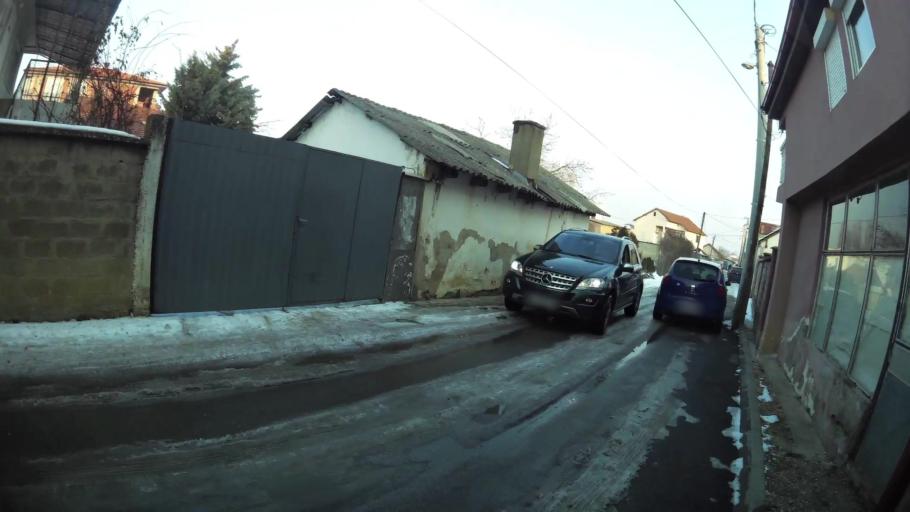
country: MK
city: Creshevo
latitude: 42.0173
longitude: 21.5132
